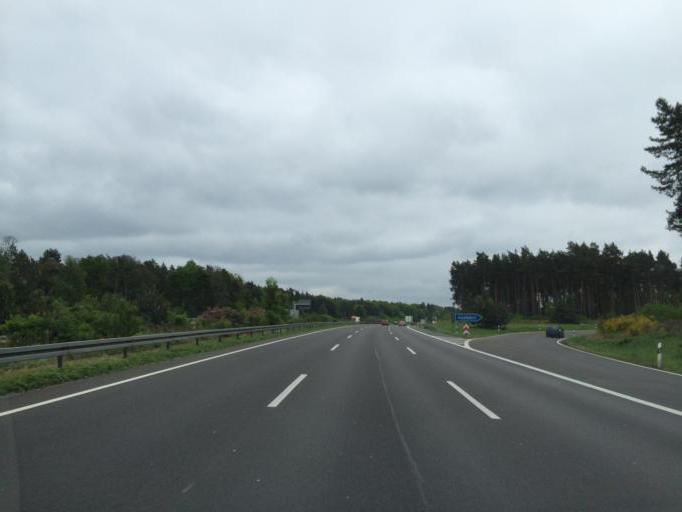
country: DE
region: Lower Saxony
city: Mariental
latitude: 52.2636
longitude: 10.9835
